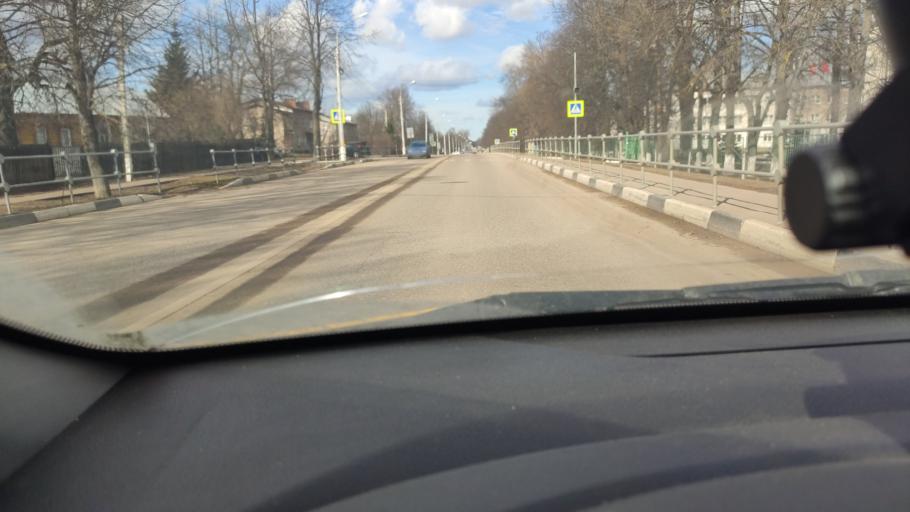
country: RU
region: Moskovskaya
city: Ruza
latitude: 55.7053
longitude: 36.1878
